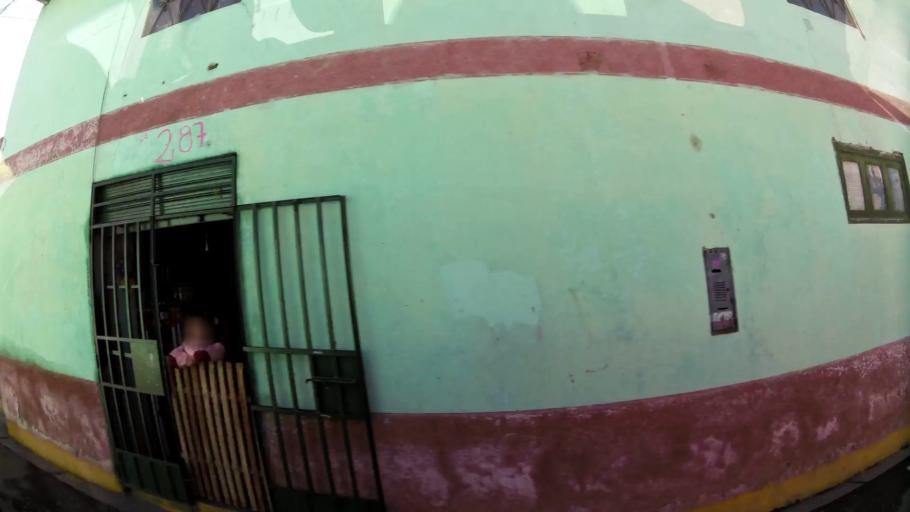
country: PE
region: Junin
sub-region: Provincia de Concepcion
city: Concepcion
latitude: -11.9161
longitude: -75.3173
